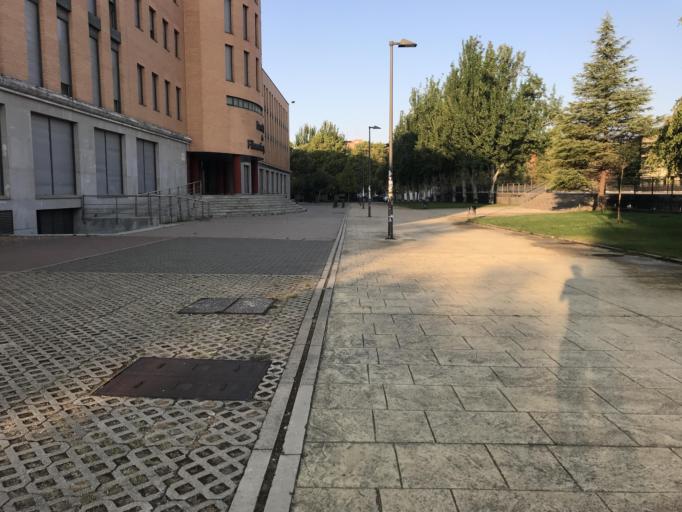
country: ES
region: Castille and Leon
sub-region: Provincia de Valladolid
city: Valladolid
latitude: 41.6584
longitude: -4.7128
